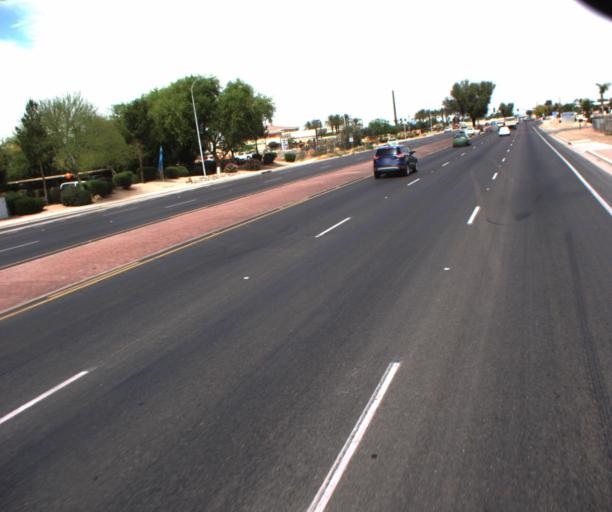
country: US
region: Arizona
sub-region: Maricopa County
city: Chandler
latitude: 33.2740
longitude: -111.8415
